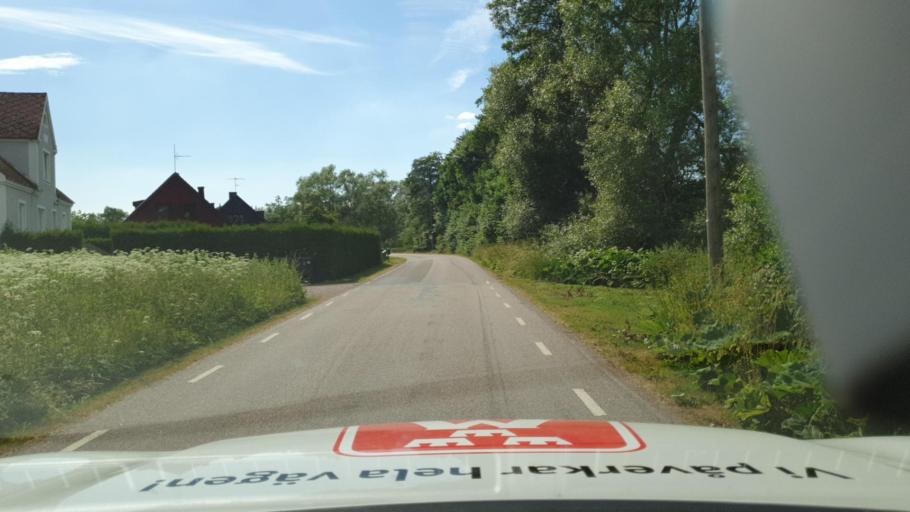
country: SE
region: Skane
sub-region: Sjobo Kommun
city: Sjoebo
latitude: 55.6377
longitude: 13.7794
